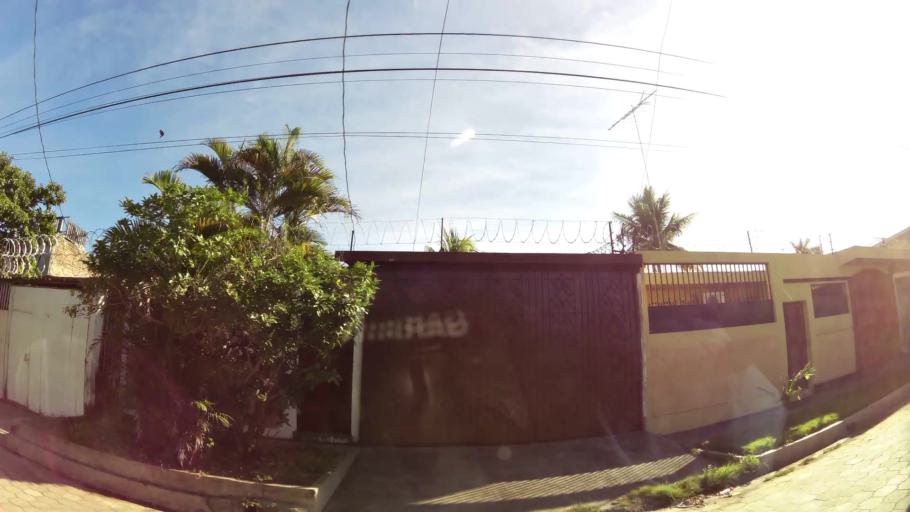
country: SV
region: San Miguel
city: San Miguel
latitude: 13.4762
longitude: -88.1941
